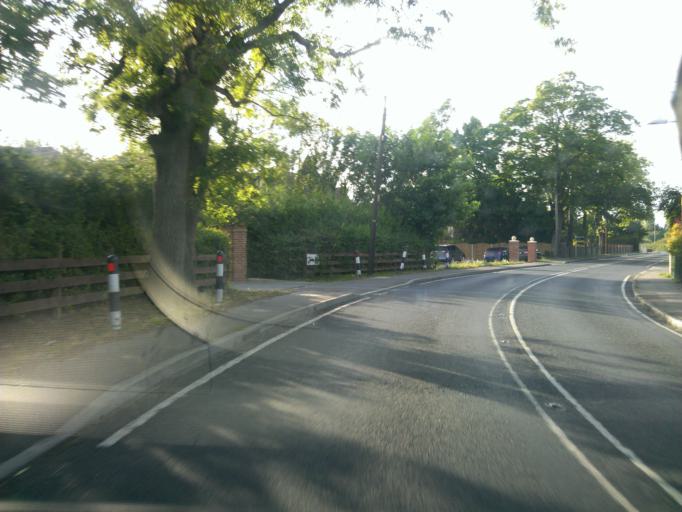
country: GB
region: England
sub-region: Essex
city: Little Clacton
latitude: 51.8399
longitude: 1.1298
